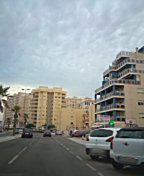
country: ES
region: Murcia
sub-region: Murcia
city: La Manga del Mar Menor
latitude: 37.7084
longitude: -0.7425
